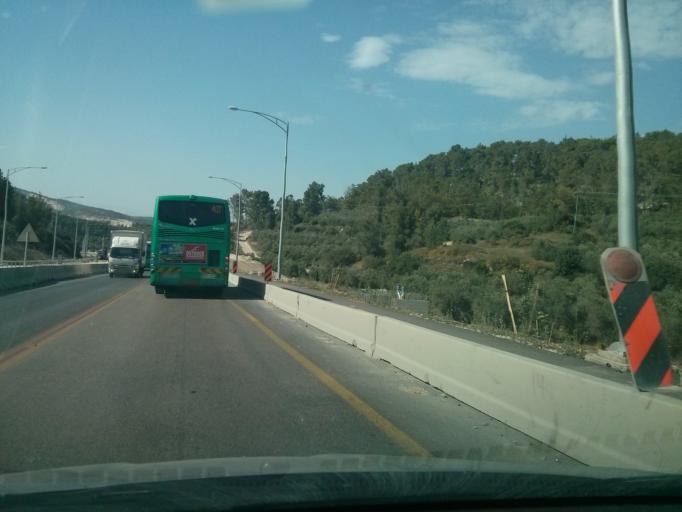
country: IL
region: Jerusalem
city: Bet Shemesh
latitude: 31.7895
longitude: 35.0137
